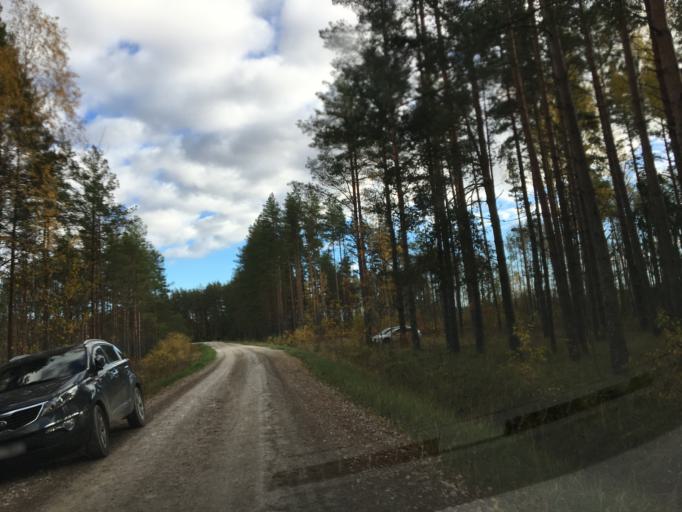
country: EE
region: Tartu
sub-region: Puhja vald
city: Puhja
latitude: 58.4345
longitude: 26.2730
